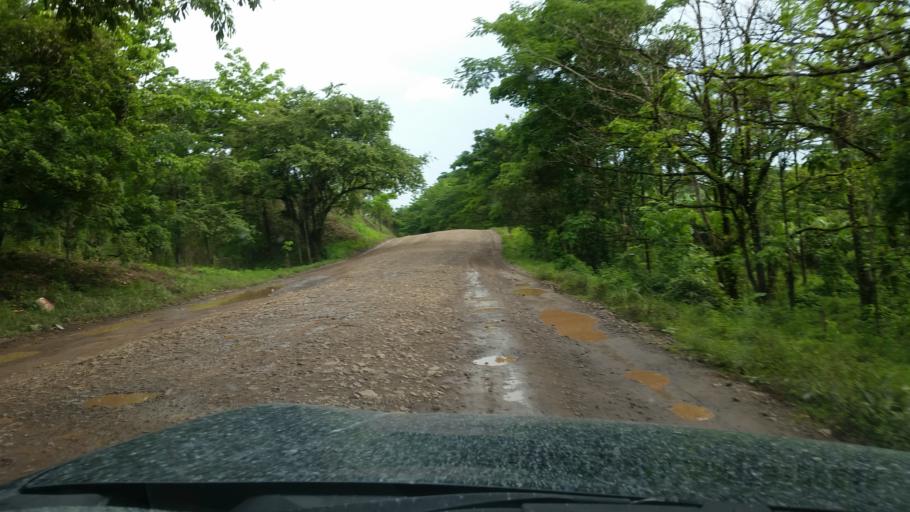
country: NI
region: Atlantico Norte (RAAN)
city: Siuna
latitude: 13.4635
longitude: -84.8487
